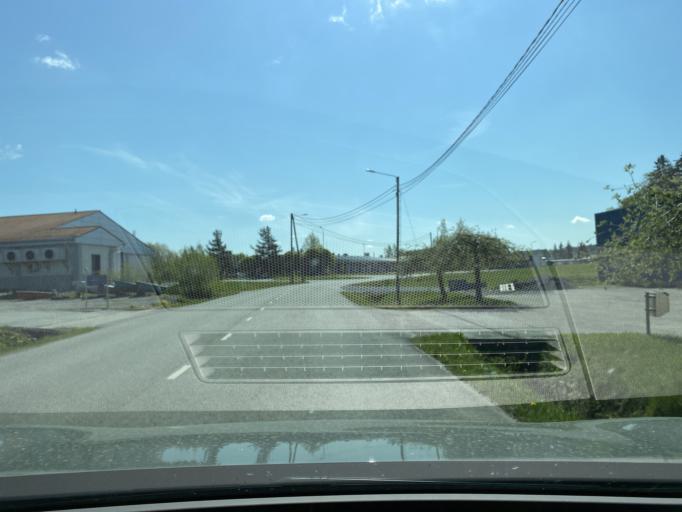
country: FI
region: Pirkanmaa
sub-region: Lounais-Pirkanmaa
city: Vammala
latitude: 61.3271
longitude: 22.9145
